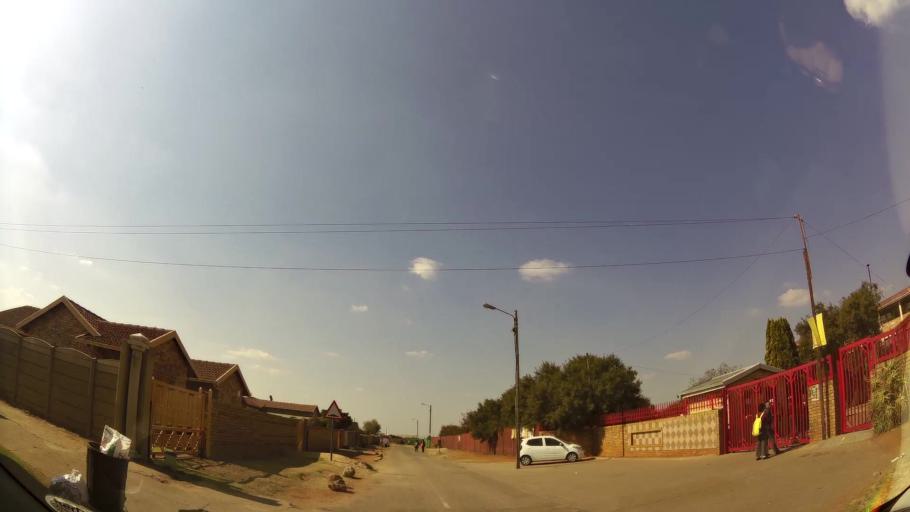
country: ZA
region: Gauteng
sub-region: Ekurhuleni Metropolitan Municipality
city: Benoni
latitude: -26.1494
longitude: 28.3984
